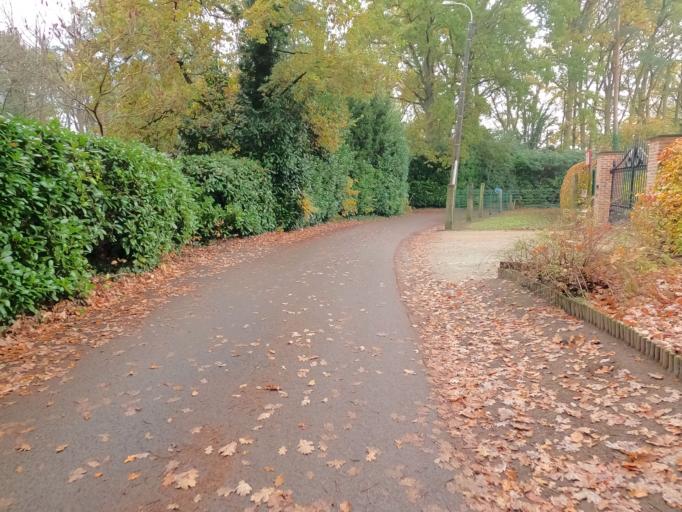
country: BE
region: Flanders
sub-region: Provincie Antwerpen
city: Nijlen
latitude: 51.1636
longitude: 4.6522
